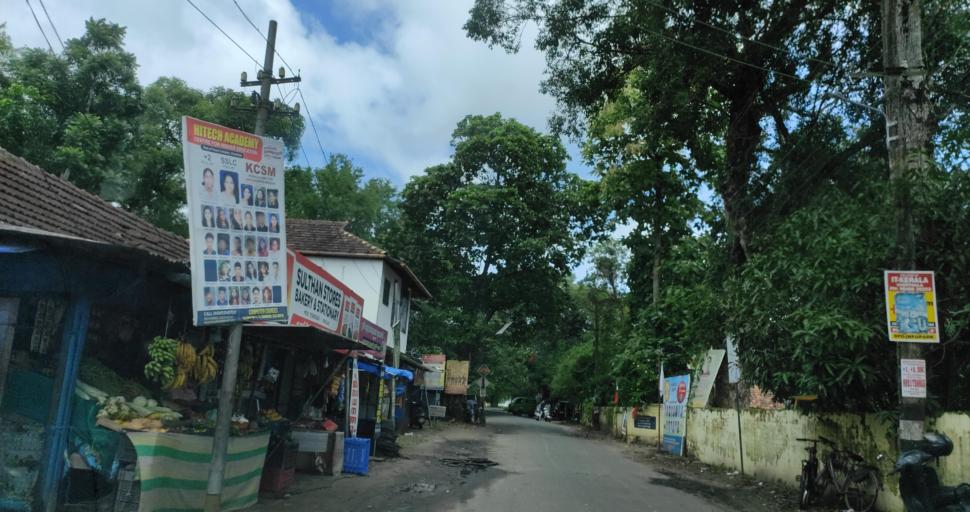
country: IN
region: Kerala
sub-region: Alappuzha
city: Vayalar
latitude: 9.7186
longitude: 76.3373
